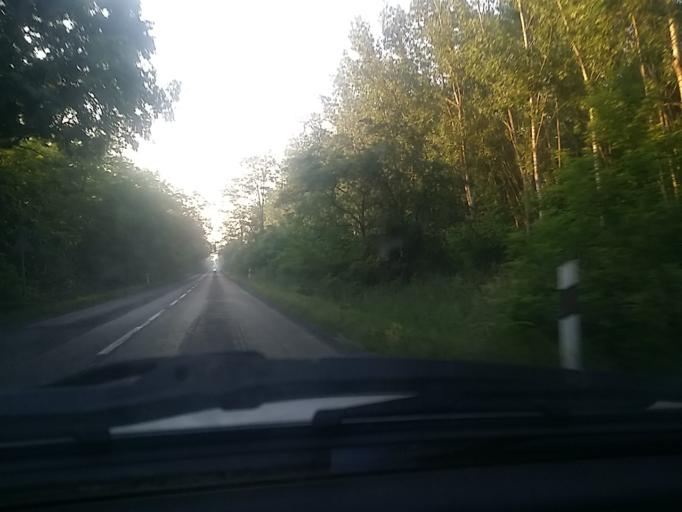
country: HU
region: Pest
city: Forropuszta
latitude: 47.4634
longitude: 19.6519
